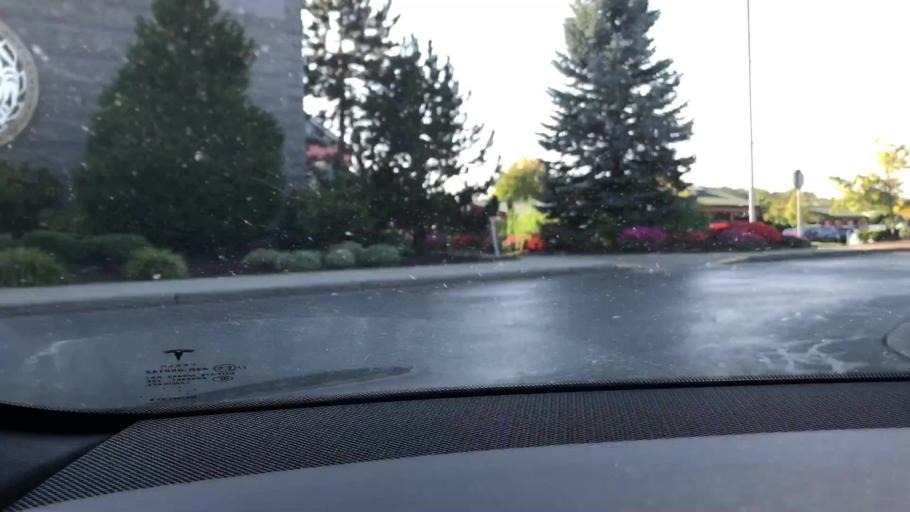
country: US
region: Washington
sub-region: Snohomish County
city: Marysville
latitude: 48.0886
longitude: -122.1888
